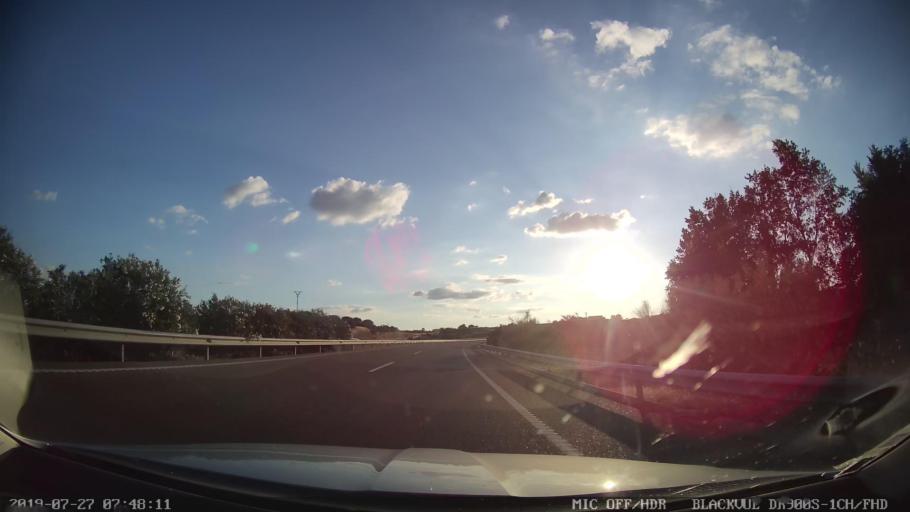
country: ES
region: Extremadura
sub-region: Provincia de Badajoz
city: San Pedro de Merida
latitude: 38.9457
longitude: -6.1810
